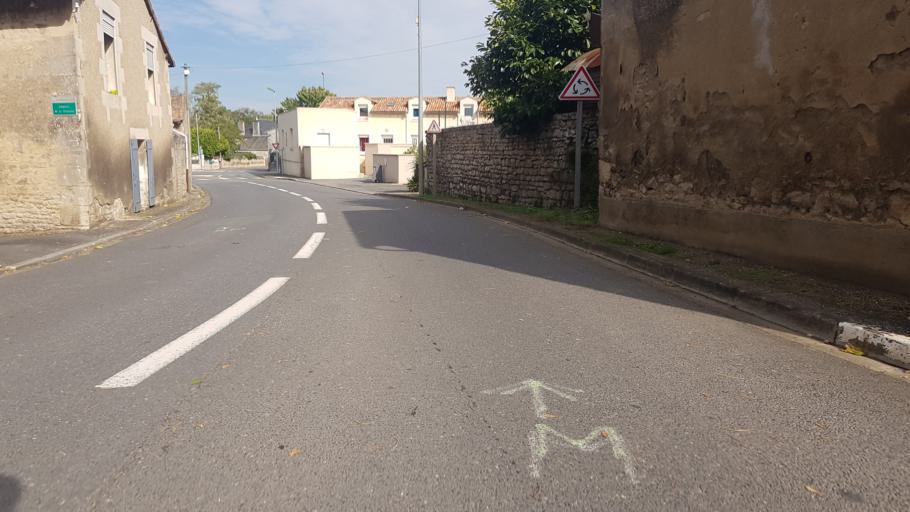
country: FR
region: Poitou-Charentes
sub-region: Departement de la Vienne
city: Chasseneuil-du-Poitou
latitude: 46.6305
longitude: 0.3694
